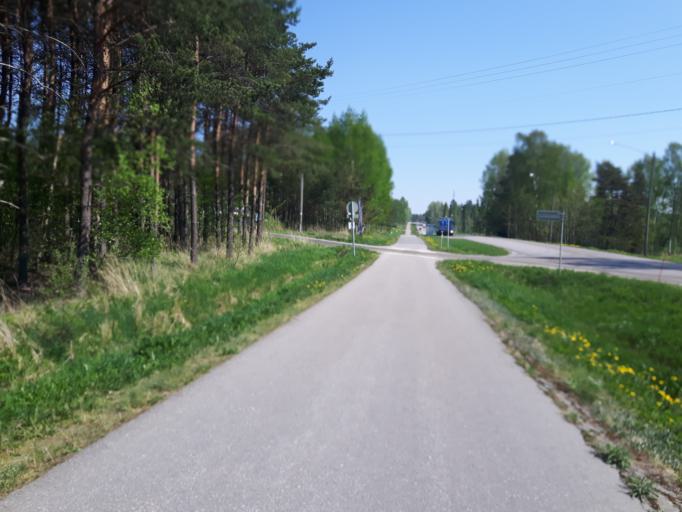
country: FI
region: Uusimaa
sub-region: Helsinki
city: Sibbo
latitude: 60.2639
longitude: 25.2683
